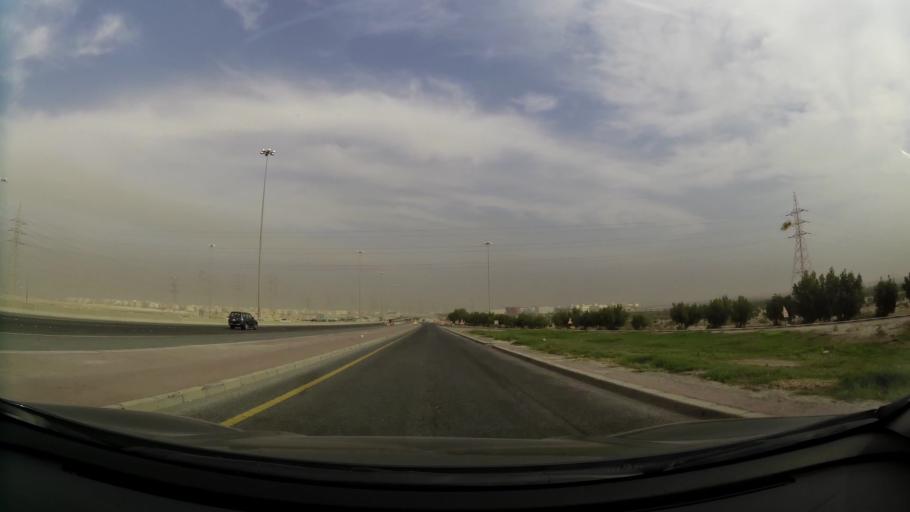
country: KW
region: Muhafazat al Jahra'
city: Al Jahra'
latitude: 29.3149
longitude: 47.7855
